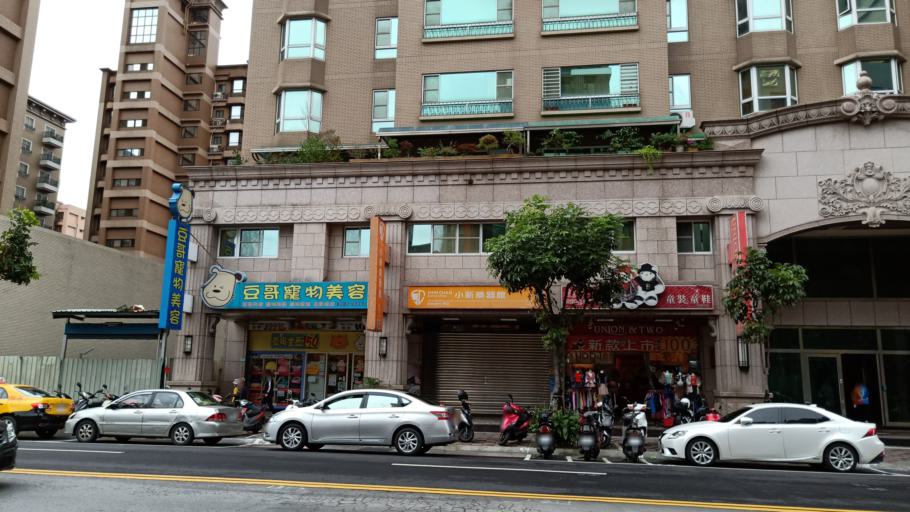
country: TW
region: Taipei
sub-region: Taipei
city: Banqiao
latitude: 25.0856
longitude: 121.4606
